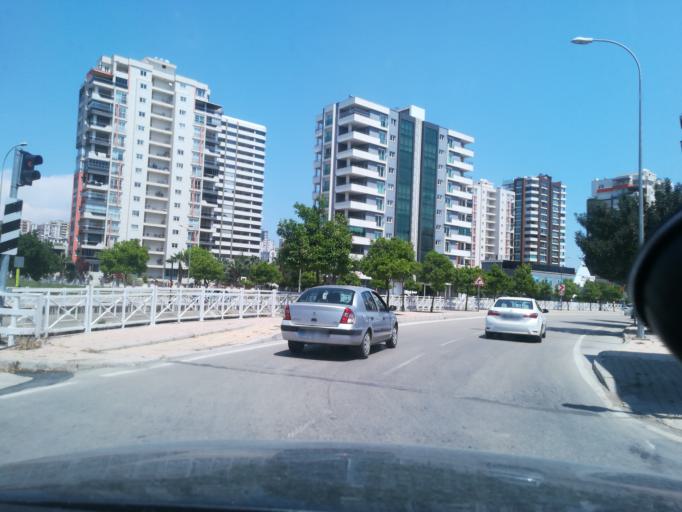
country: TR
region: Adana
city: Seyhan
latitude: 37.0269
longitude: 35.2597
